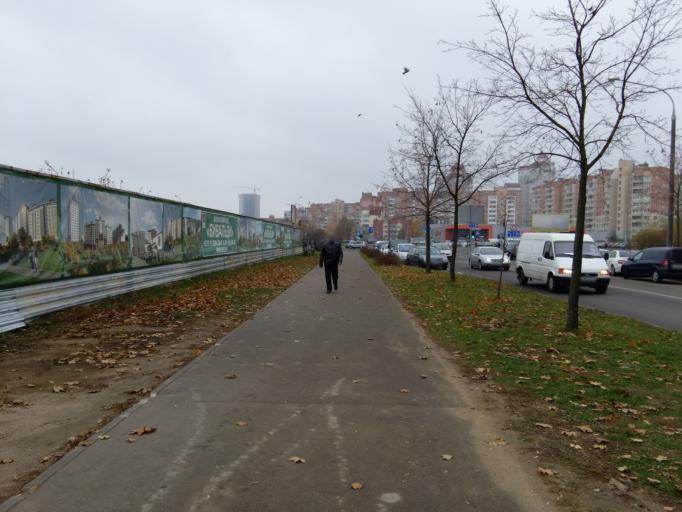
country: BY
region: Minsk
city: Borovlyany
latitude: 53.9481
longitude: 27.6821
